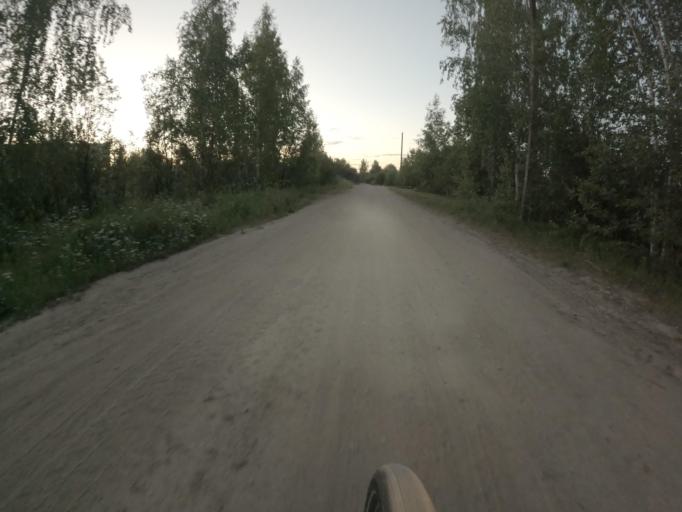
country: RU
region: St.-Petersburg
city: Sapernyy
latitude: 59.7802
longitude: 30.6725
